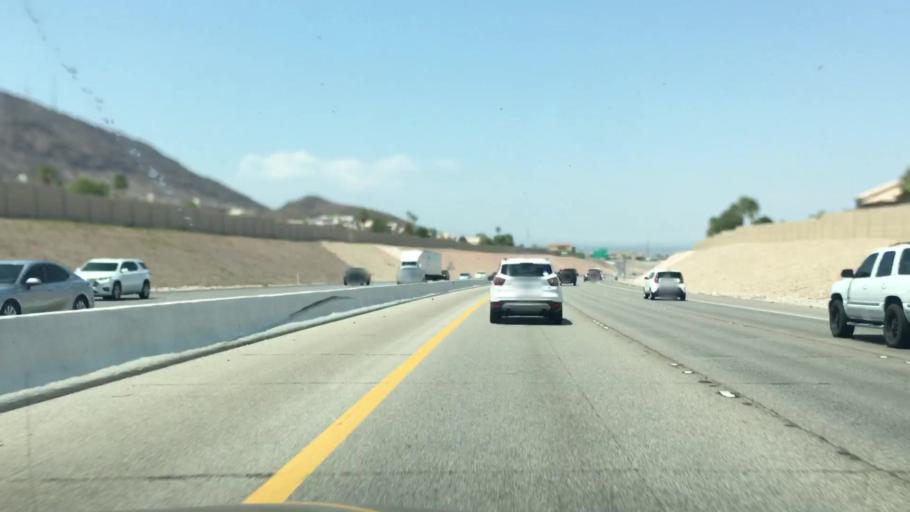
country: US
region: Nevada
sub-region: Clark County
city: Henderson
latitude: 36.0045
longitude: -114.9841
